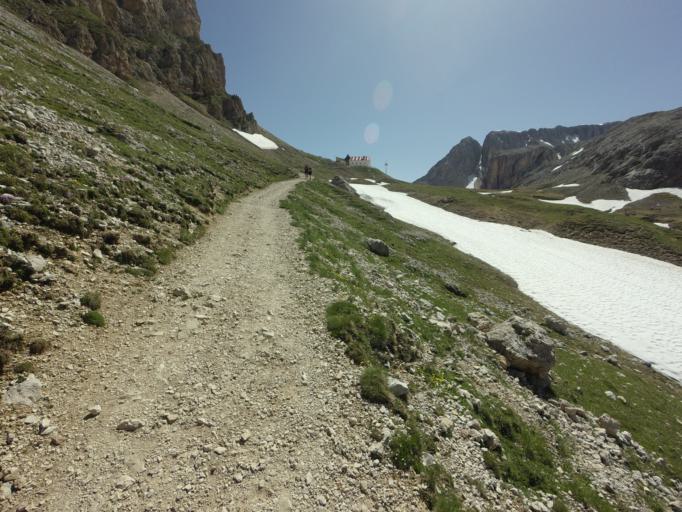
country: IT
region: Trentino-Alto Adige
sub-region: Provincia di Trento
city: Mazzin
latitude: 46.4971
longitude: 11.6294
